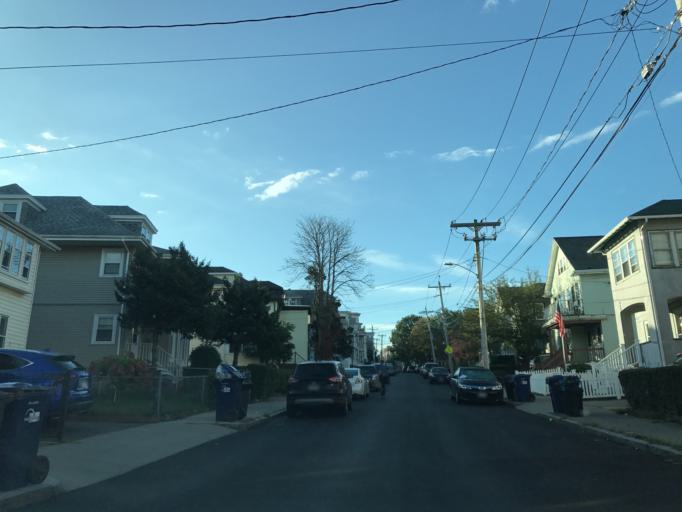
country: US
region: Massachusetts
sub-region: Suffolk County
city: South Boston
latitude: 42.2955
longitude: -71.0553
